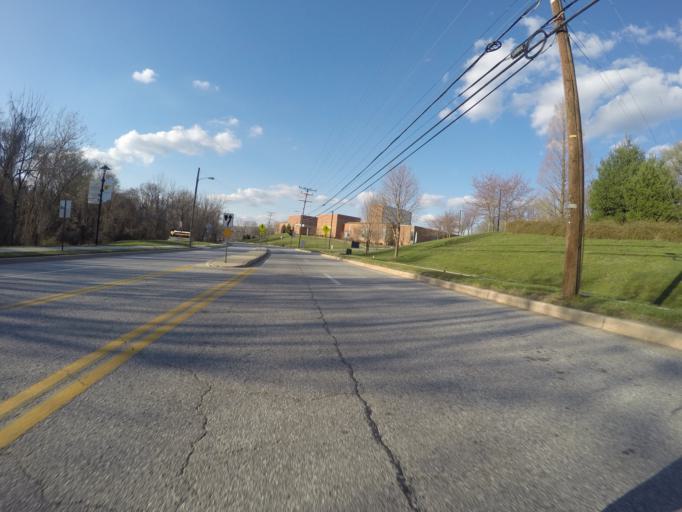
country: US
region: Maryland
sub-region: Baltimore County
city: Towson
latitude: 39.3886
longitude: -76.6132
